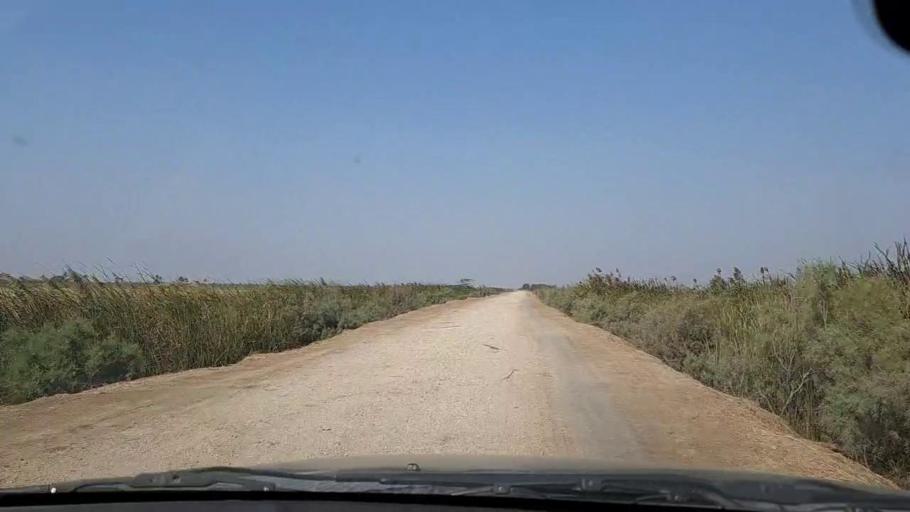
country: PK
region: Sindh
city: Mirpur Sakro
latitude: 24.3542
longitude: 67.6831
